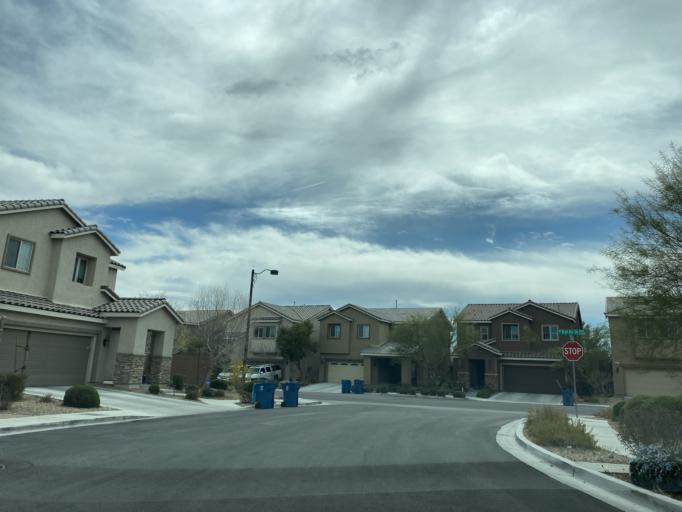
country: US
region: Nevada
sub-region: Clark County
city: Summerlin South
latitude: 36.3075
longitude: -115.2996
